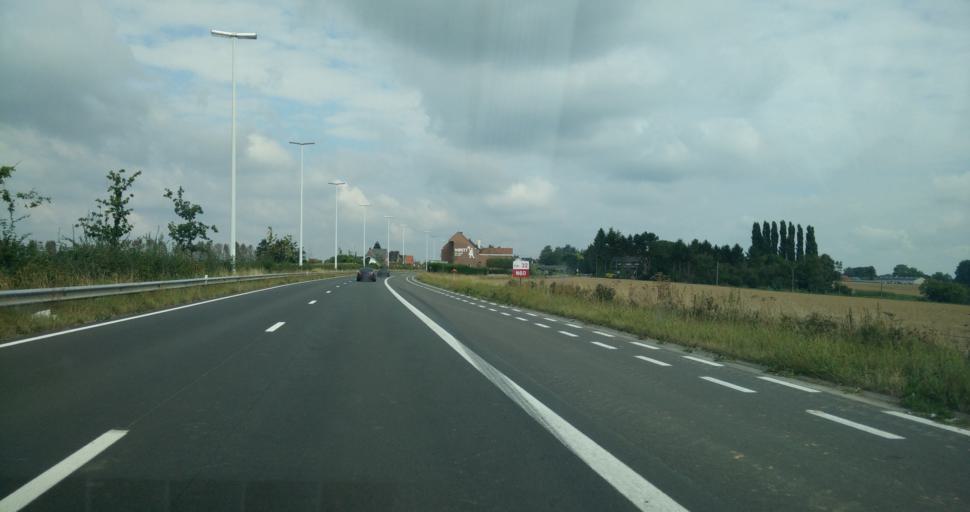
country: BE
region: Flanders
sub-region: Provincie Oost-Vlaanderen
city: Ronse
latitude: 50.7809
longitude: 3.5900
